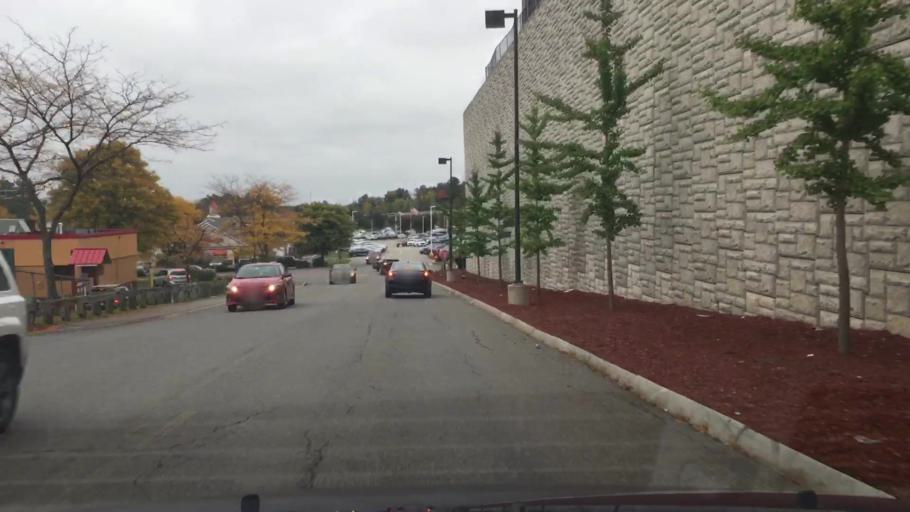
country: US
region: New Hampshire
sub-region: Hillsborough County
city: Hudson
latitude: 42.7265
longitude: -71.4477
